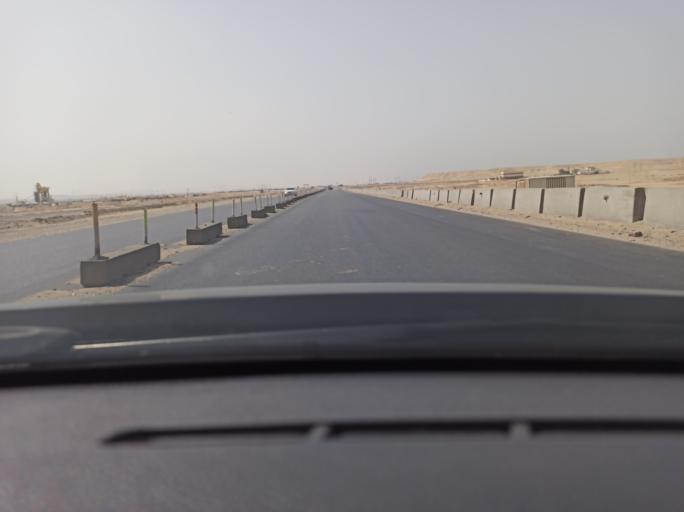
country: EG
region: Muhafazat al Fayyum
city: Al Wasitah
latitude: 29.2906
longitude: 31.2736
